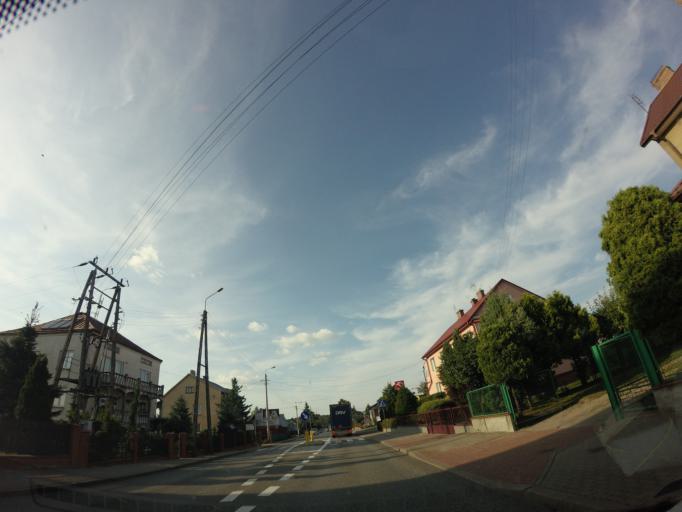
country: PL
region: Podlasie
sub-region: Powiat sokolski
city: Suchowola
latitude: 53.5824
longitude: 23.1070
